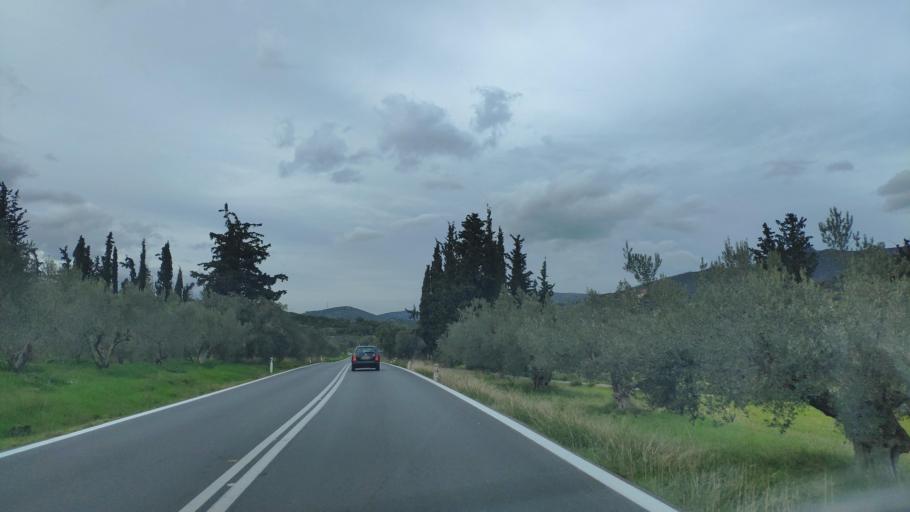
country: GR
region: Peloponnese
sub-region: Nomos Argolidos
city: Koutsopodi
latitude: 37.7569
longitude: 22.7325
